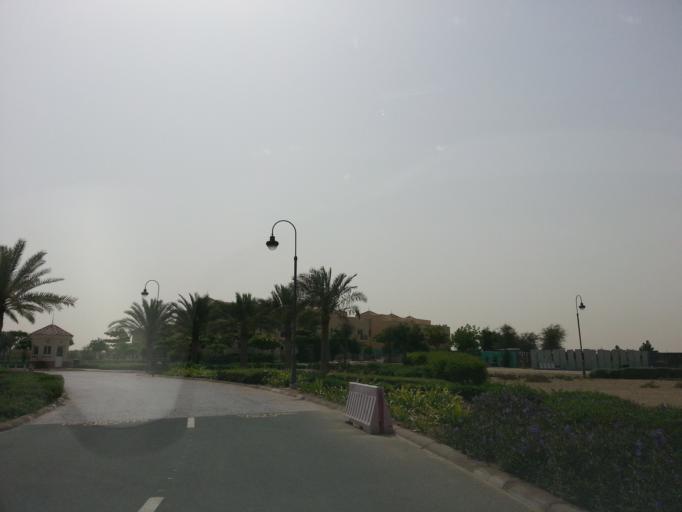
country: AE
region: Dubai
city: Dubai
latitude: 25.0339
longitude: 55.2078
